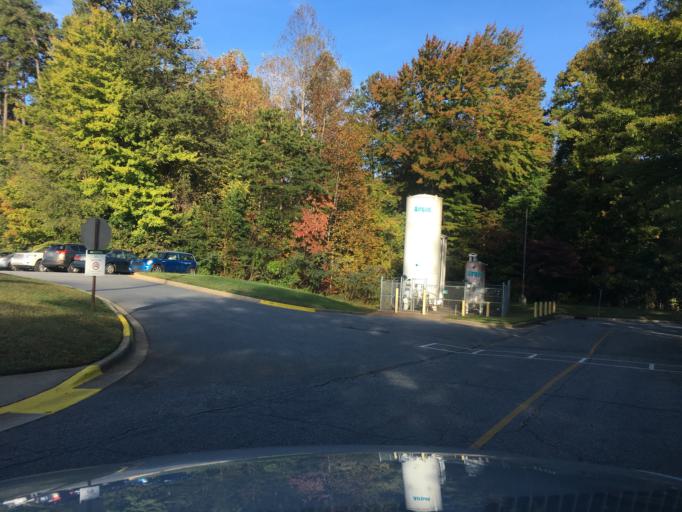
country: US
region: North Carolina
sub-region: Catawba County
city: Conover
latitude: 35.7139
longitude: -81.2687
